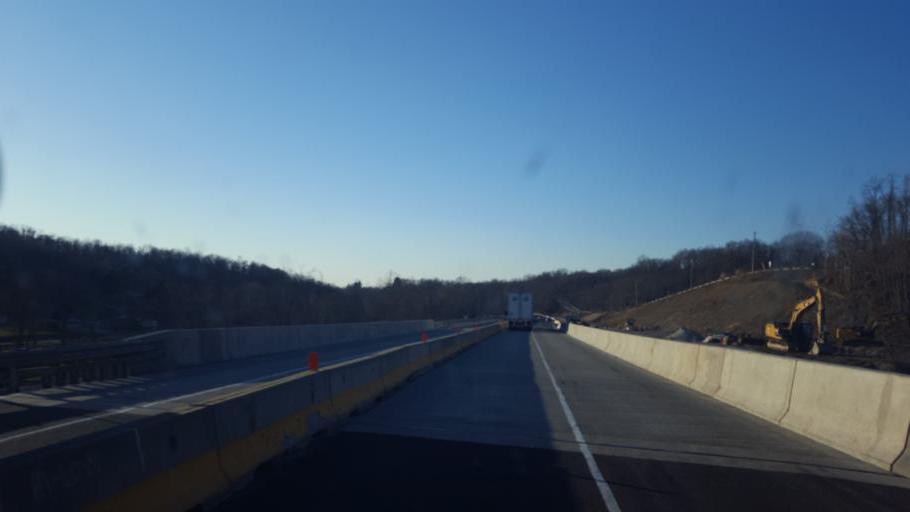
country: US
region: Pennsylvania
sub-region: Washington County
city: Bentleyville
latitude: 40.1247
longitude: -79.9578
